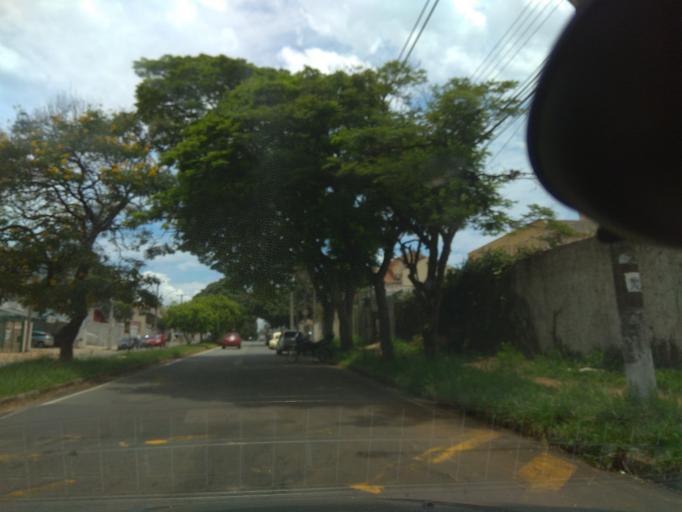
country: BR
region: Sao Paulo
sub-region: Campinas
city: Campinas
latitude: -22.8288
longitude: -47.0744
